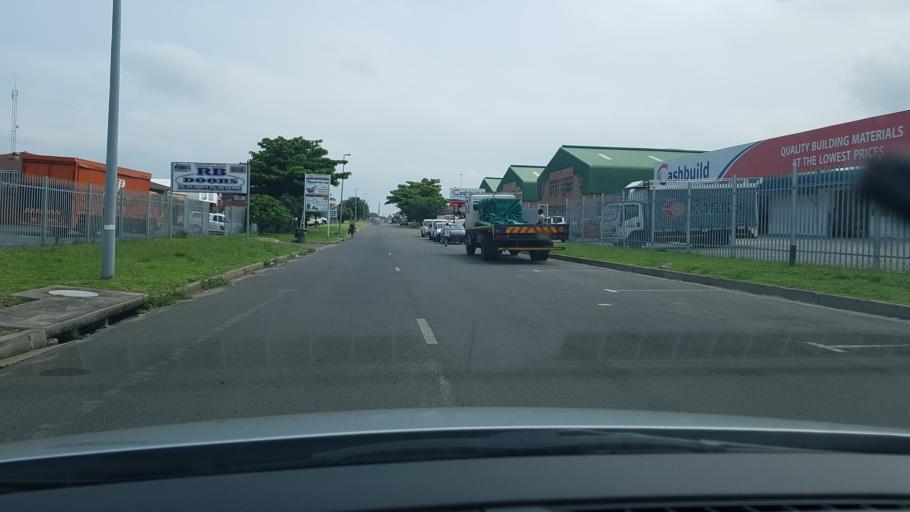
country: ZA
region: KwaZulu-Natal
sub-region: uThungulu District Municipality
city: Richards Bay
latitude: -28.7447
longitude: 32.0487
